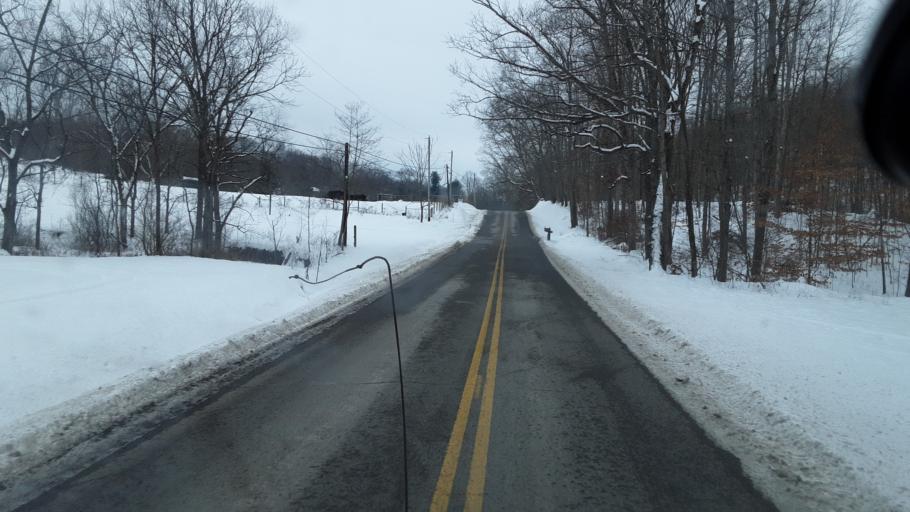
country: US
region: Ohio
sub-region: Perry County
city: Somerset
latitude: 39.9085
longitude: -82.2282
